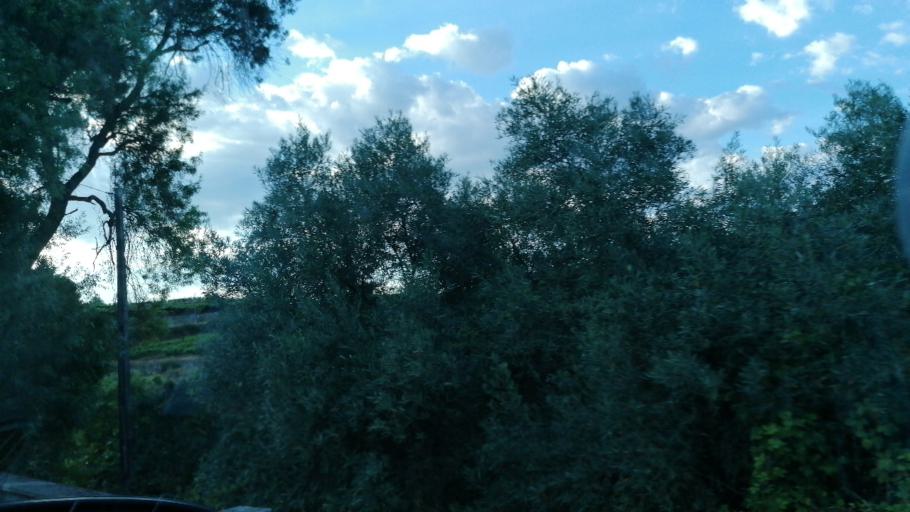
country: PT
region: Viseu
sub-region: Sao Joao da Pesqueira
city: Sao Joao da Pesqueira
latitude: 41.2512
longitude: -7.4353
